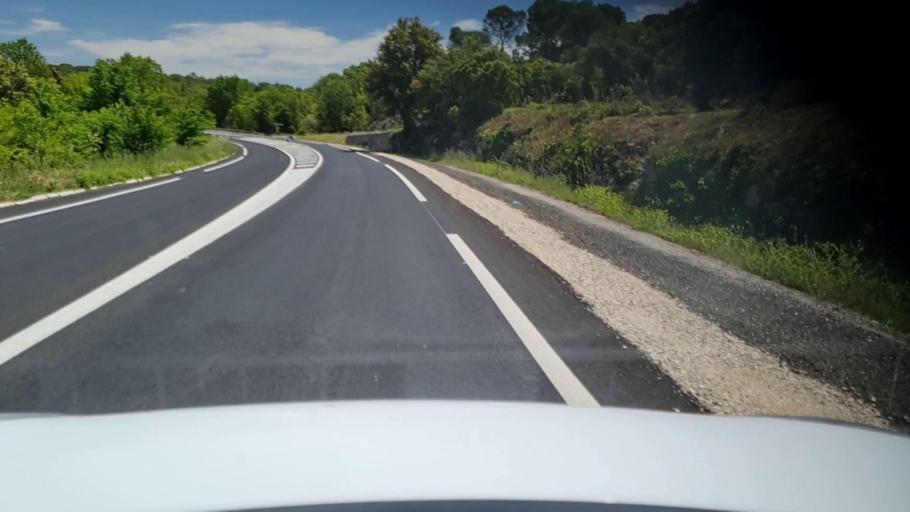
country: FR
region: Languedoc-Roussillon
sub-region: Departement du Gard
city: Villevieille
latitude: 43.7886
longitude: 4.1083
